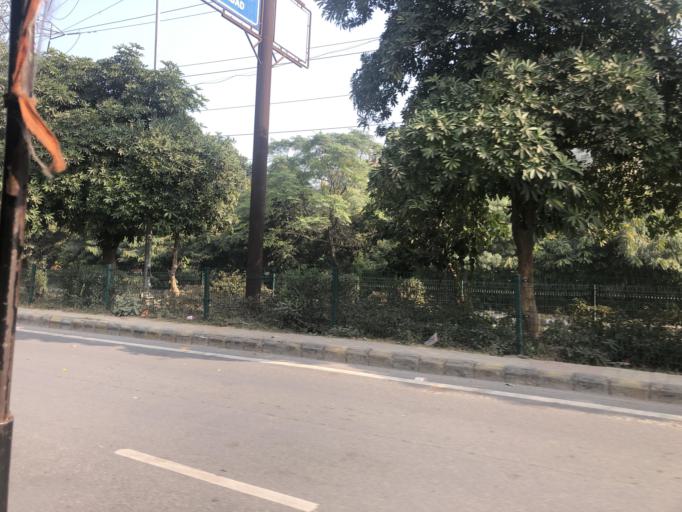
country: IN
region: Haryana
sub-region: Gurgaon
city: Gurgaon
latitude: 28.4291
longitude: 77.0912
